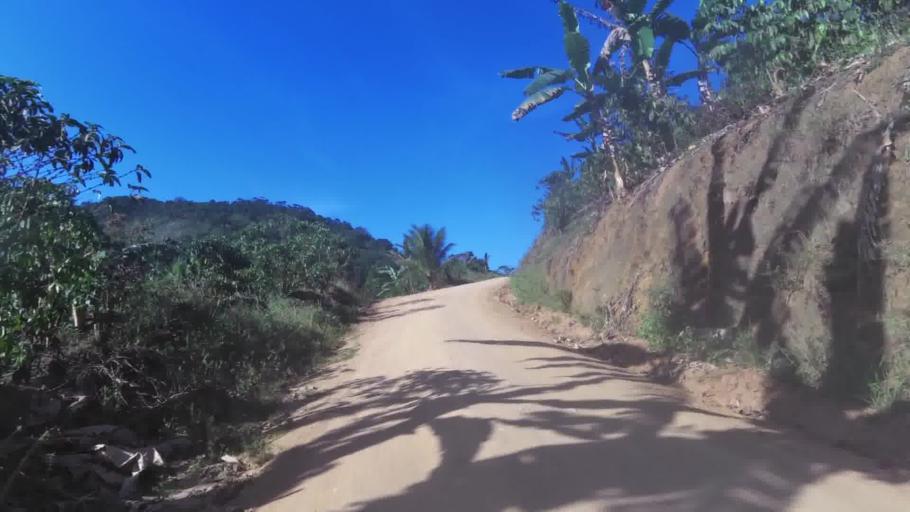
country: BR
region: Espirito Santo
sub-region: Iconha
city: Iconha
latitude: -20.7562
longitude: -40.8146
